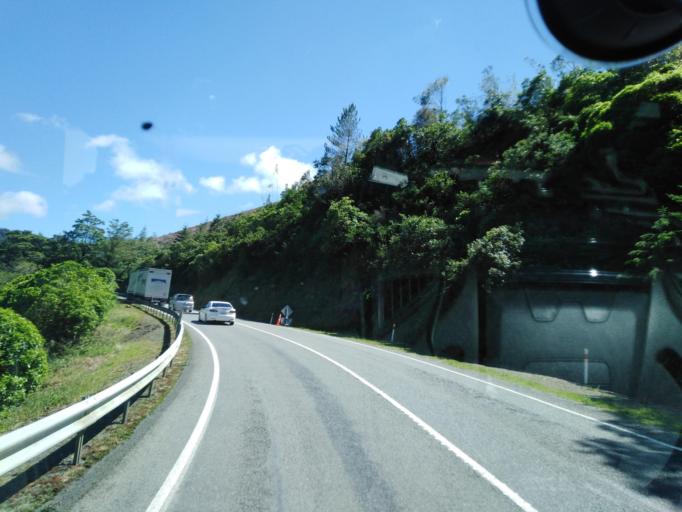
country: NZ
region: Nelson
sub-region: Nelson City
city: Nelson
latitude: -41.1996
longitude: 173.5613
